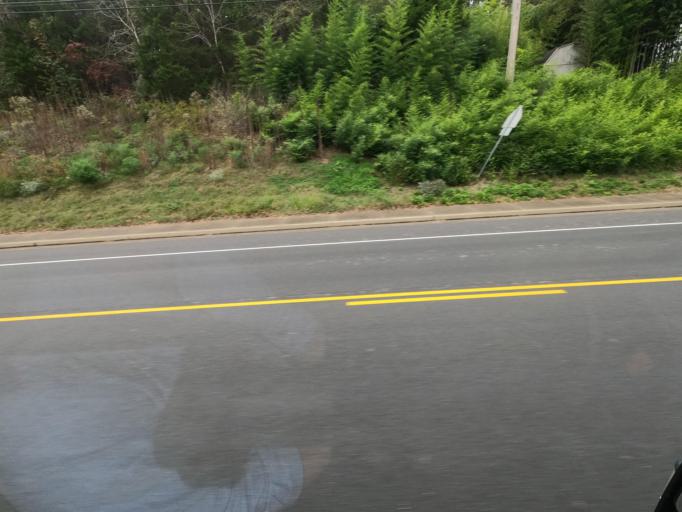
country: US
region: Tennessee
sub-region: Cheatham County
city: Kingston Springs
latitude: 36.0939
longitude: -87.0932
